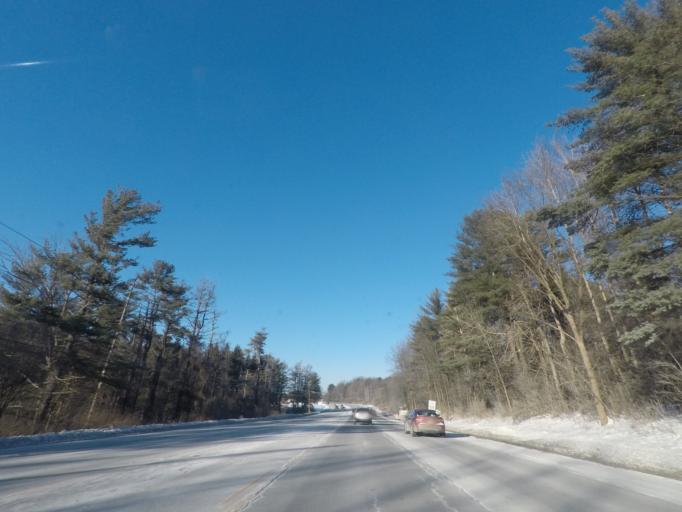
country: US
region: New York
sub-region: Saratoga County
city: Saratoga Springs
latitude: 43.0479
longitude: -73.7890
